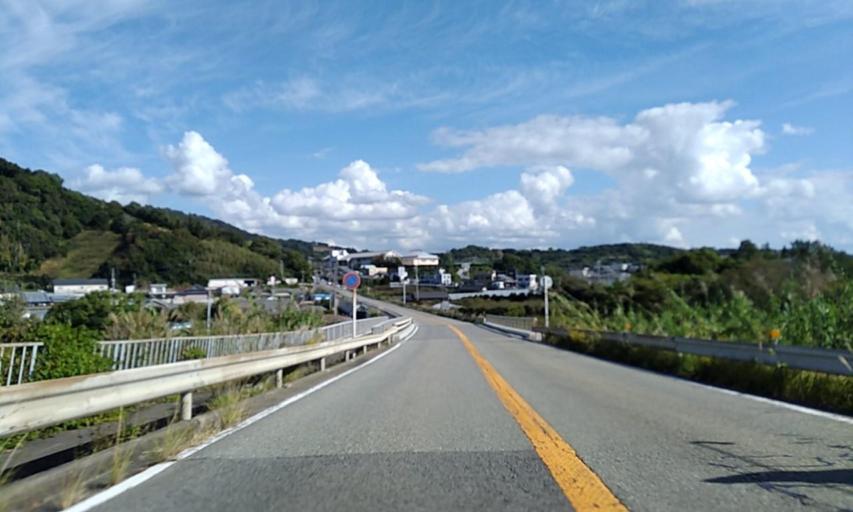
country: JP
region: Wakayama
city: Tanabe
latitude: 33.7818
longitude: 135.2757
